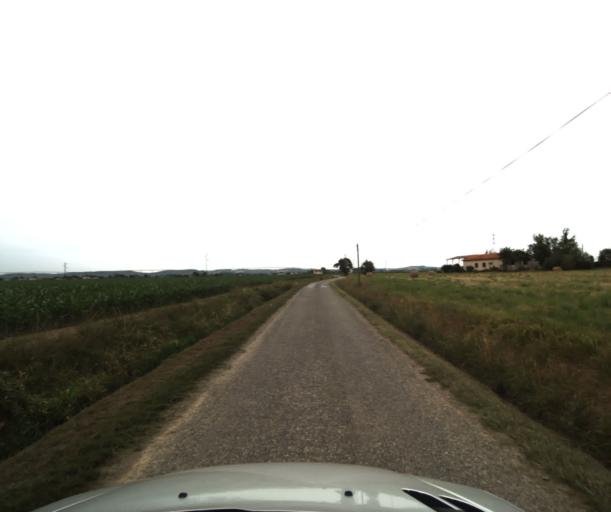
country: FR
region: Midi-Pyrenees
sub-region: Departement de la Haute-Garonne
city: Lacasse
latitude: 43.4232
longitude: 1.2567
